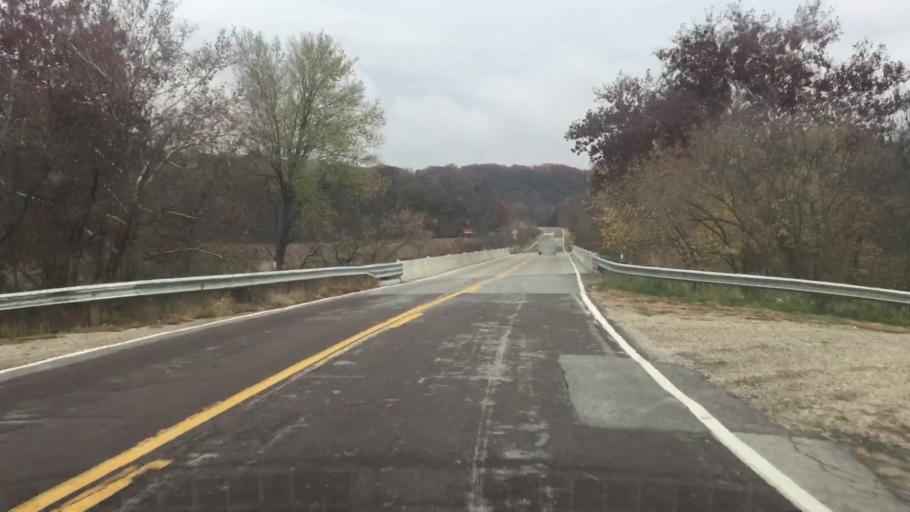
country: US
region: Missouri
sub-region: Callaway County
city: Fulton
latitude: 38.7958
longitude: -91.8773
